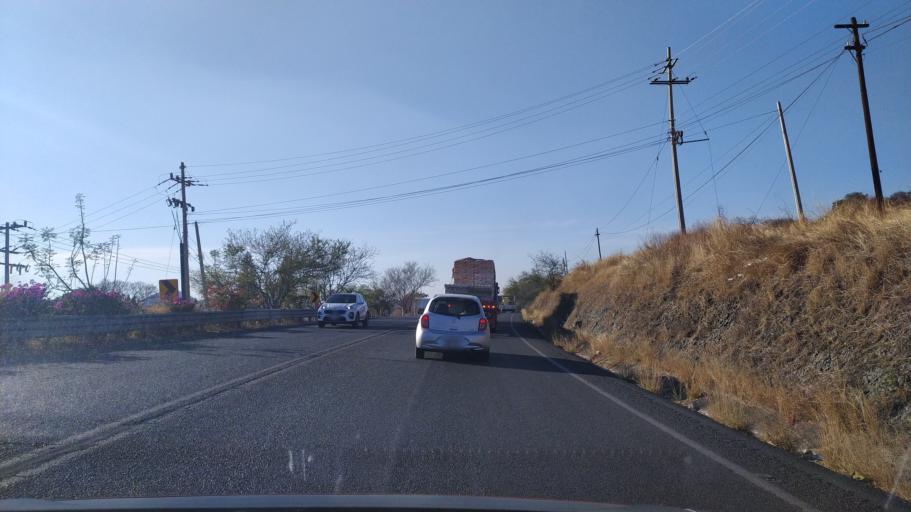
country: MX
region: Jalisco
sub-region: Poncitlan
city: Cuitzeo (La Estancia)
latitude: 20.2977
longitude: -102.7656
